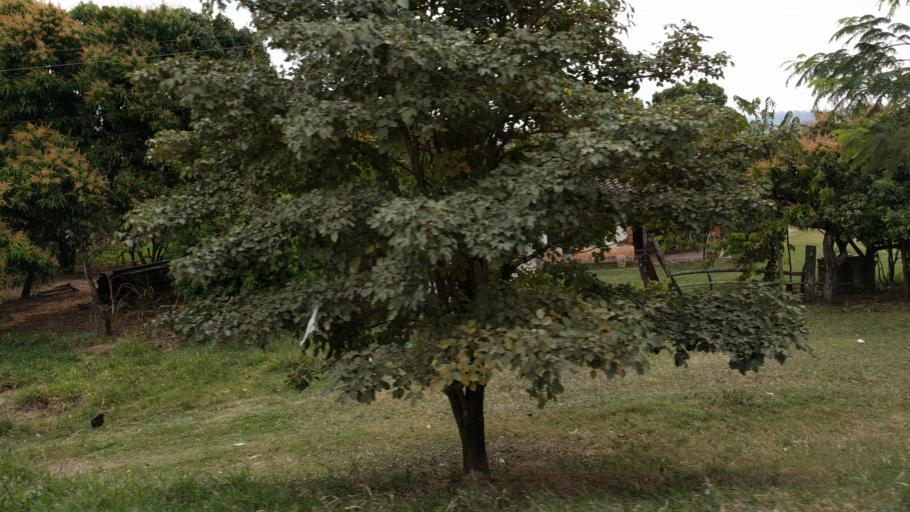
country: BO
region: Santa Cruz
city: Jorochito
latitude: -18.0466
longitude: -63.4191
